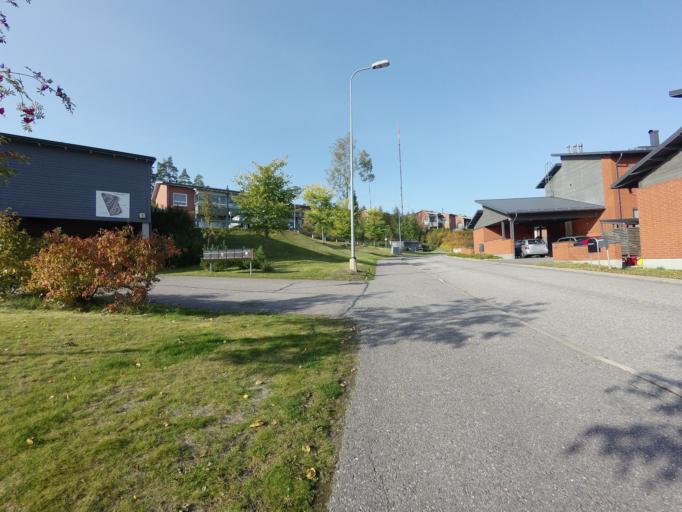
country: FI
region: Uusimaa
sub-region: Helsinki
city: Espoo
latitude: 60.1713
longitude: 24.6435
